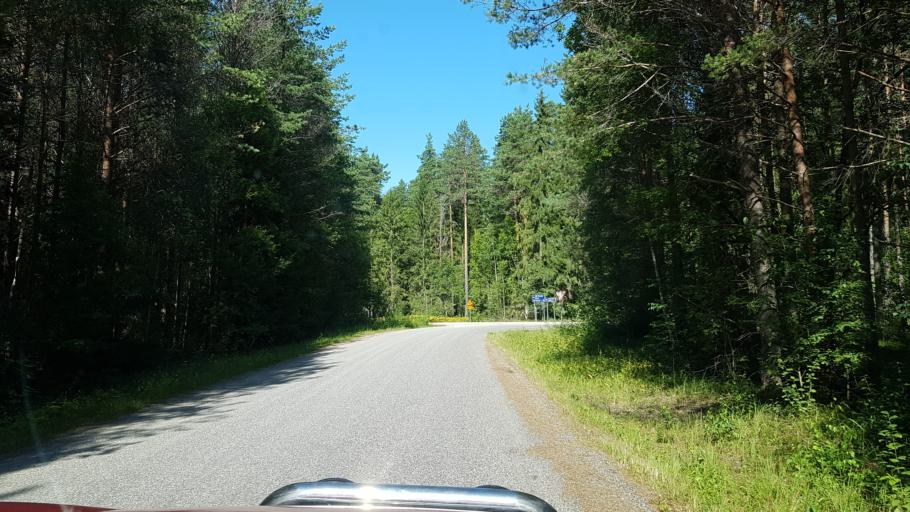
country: EE
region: Vorumaa
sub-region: Voru linn
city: Voru
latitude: 57.7346
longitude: 27.2045
